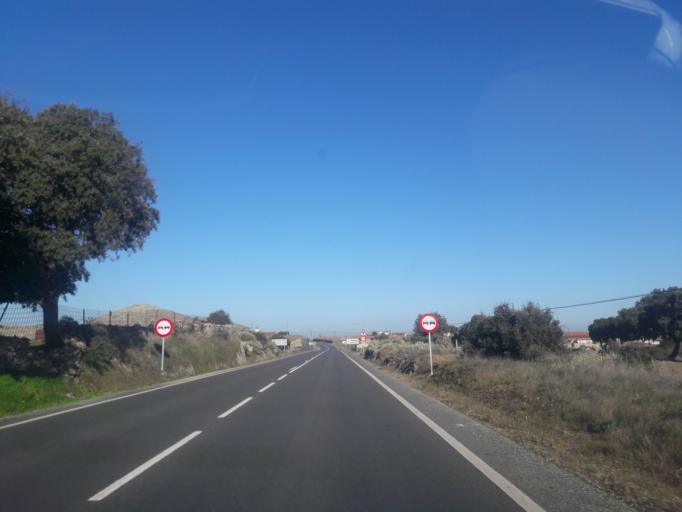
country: ES
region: Castille and Leon
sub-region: Provincia de Salamanca
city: Doninos de Ledesma
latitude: 41.0317
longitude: -6.0196
